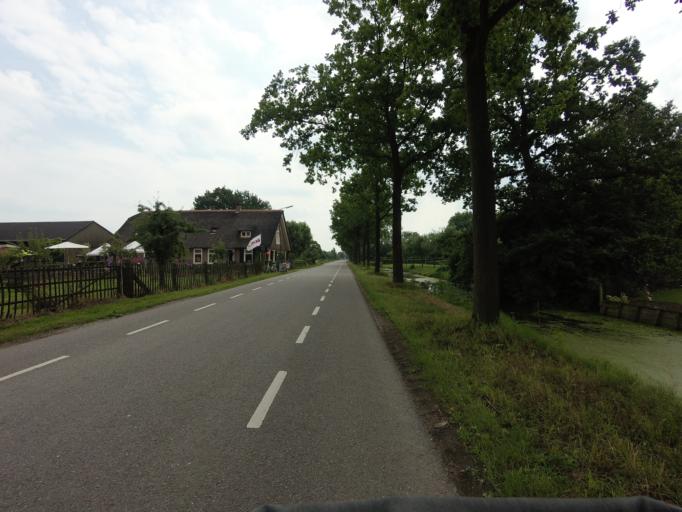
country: NL
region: Utrecht
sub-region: Gemeente Vianen
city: Vianen
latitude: 52.0066
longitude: 5.1234
